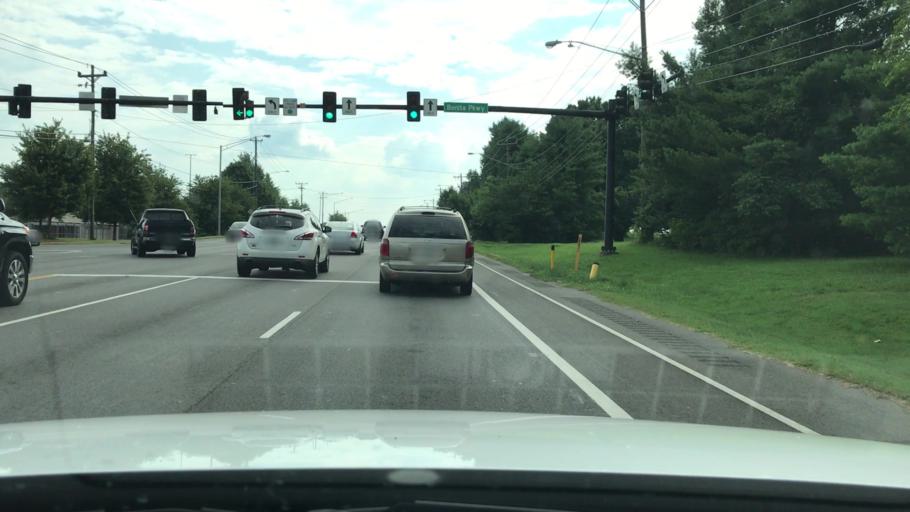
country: US
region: Tennessee
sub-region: Sumner County
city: Hendersonville
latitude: 36.3154
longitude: -86.5890
